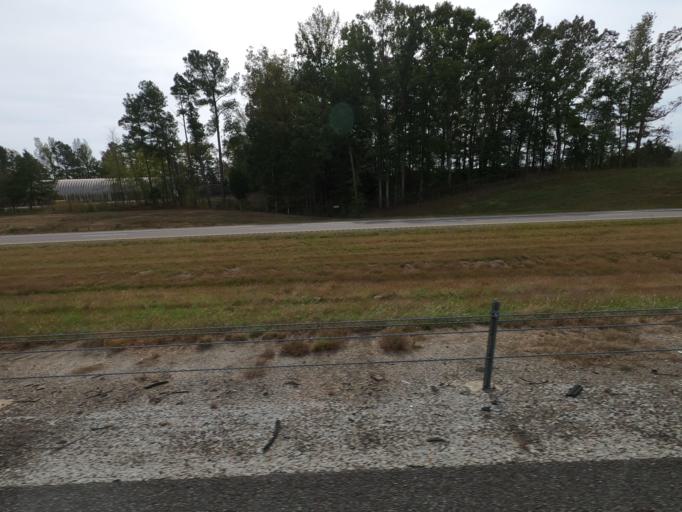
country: US
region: Tennessee
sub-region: Henderson County
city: Lexington
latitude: 35.7536
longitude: -88.5207
